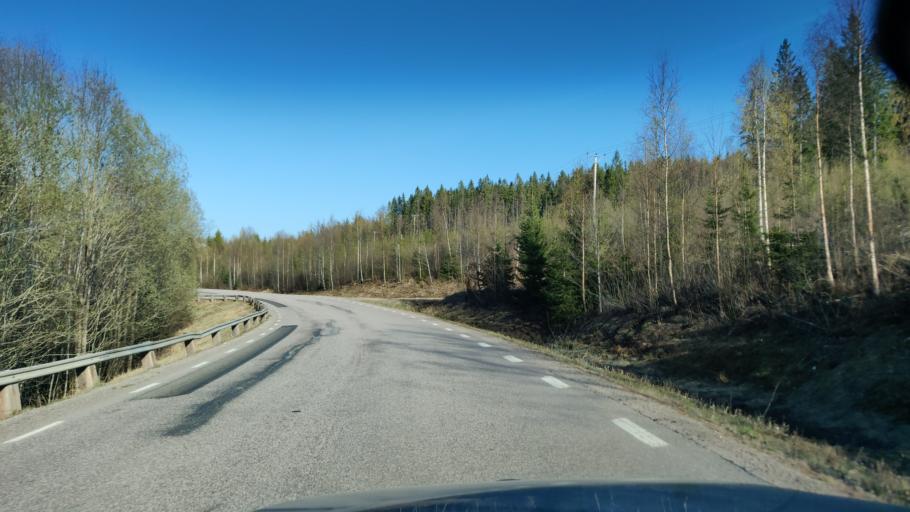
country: SE
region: Vaermland
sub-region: Munkfors Kommun
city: Munkfors
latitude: 59.9696
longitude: 13.4426
